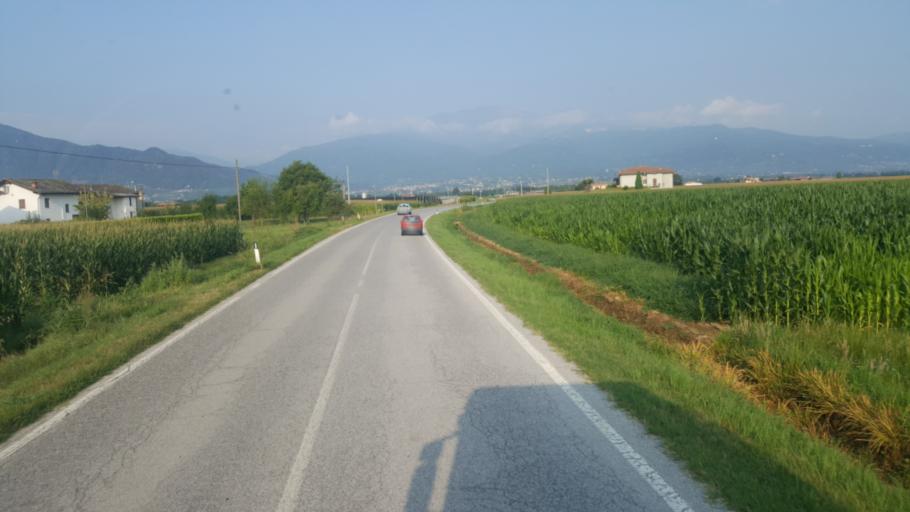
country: IT
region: Piedmont
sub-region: Provincia di Torino
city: Cavour
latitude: 44.7448
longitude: 7.3960
